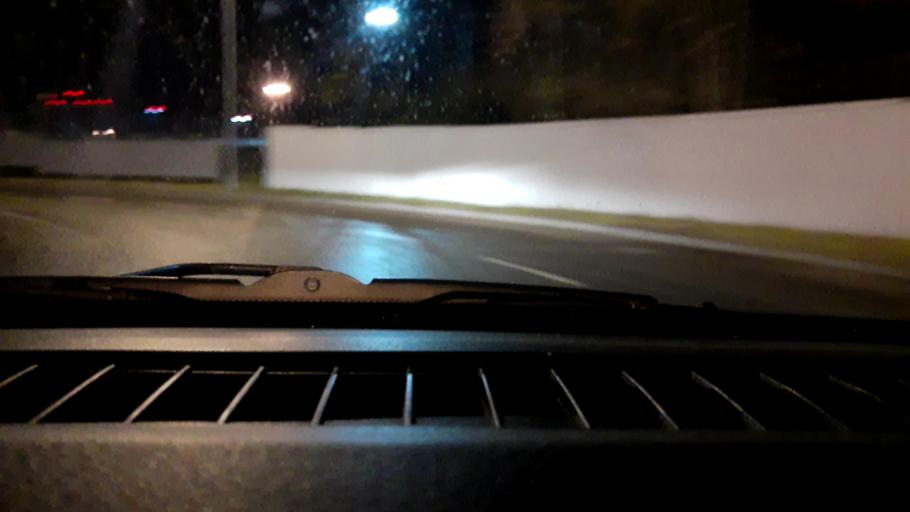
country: RU
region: Nizjnij Novgorod
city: Gorbatovka
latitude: 56.2192
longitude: 43.7955
